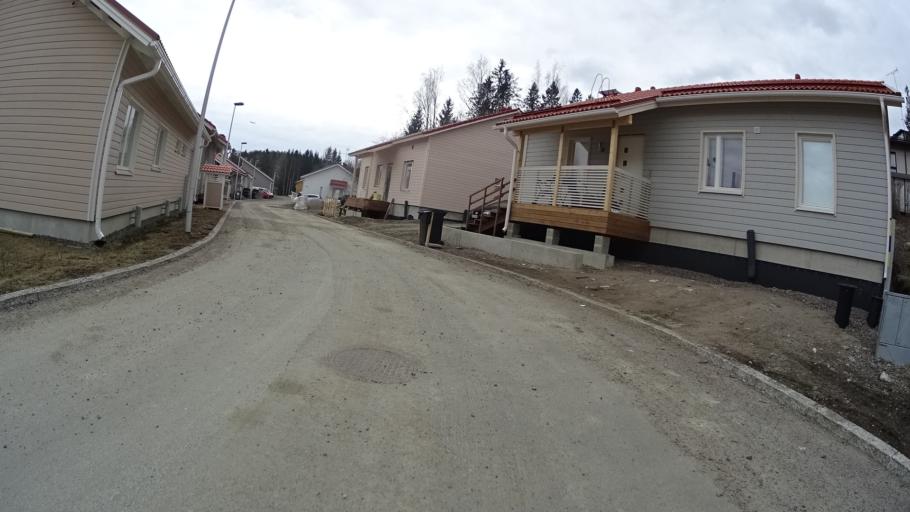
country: FI
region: Uusimaa
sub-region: Helsinki
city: Kilo
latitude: 60.2881
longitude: 24.7827
